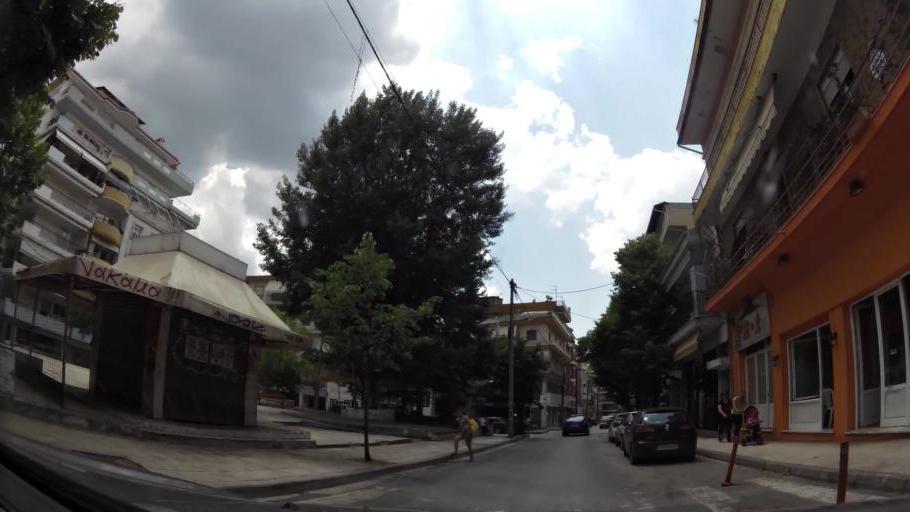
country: GR
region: West Macedonia
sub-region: Nomos Kozanis
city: Kozani
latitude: 40.3016
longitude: 21.7931
